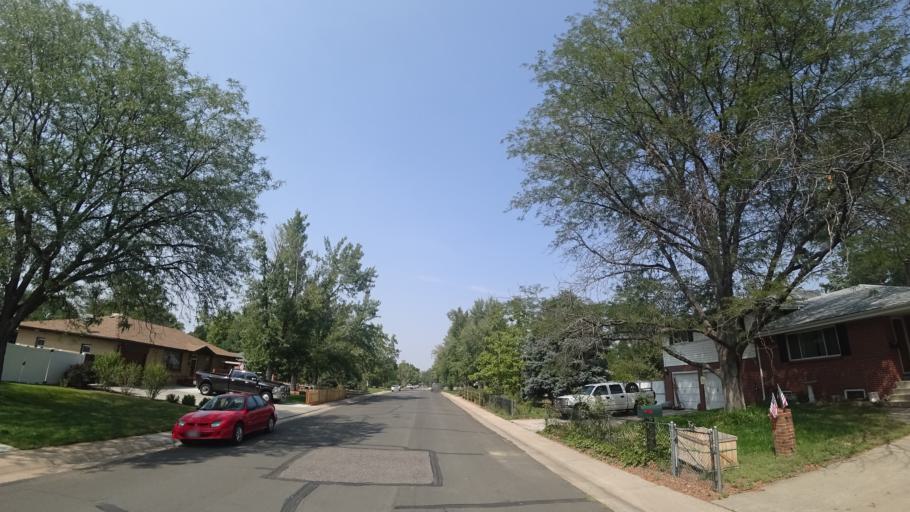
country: US
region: Colorado
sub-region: Arapahoe County
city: Englewood
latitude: 39.6314
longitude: -104.9996
